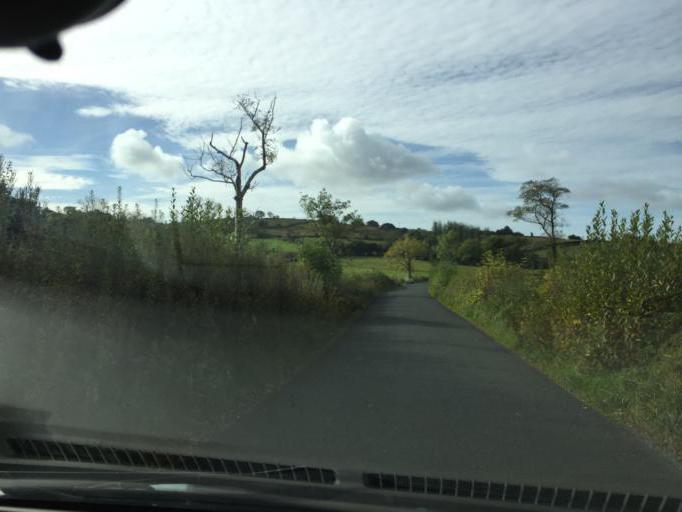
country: IE
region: Connaught
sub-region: Roscommon
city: Boyle
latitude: 54.0316
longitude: -8.3112
